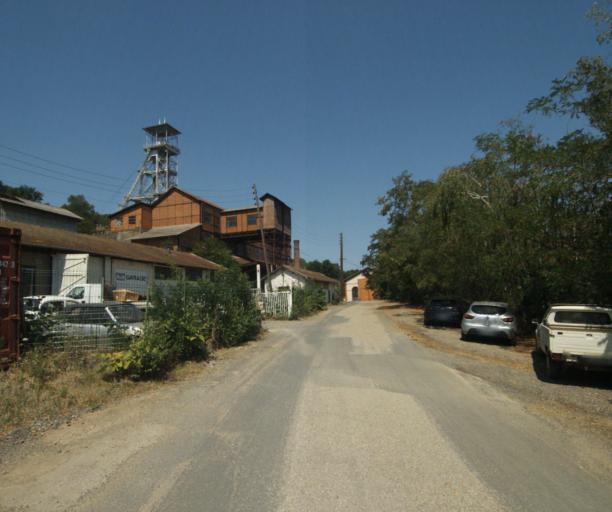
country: FR
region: Rhone-Alpes
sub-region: Departement du Rhone
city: Saint-Pierre-la-Palud
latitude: 45.7956
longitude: 4.6083
